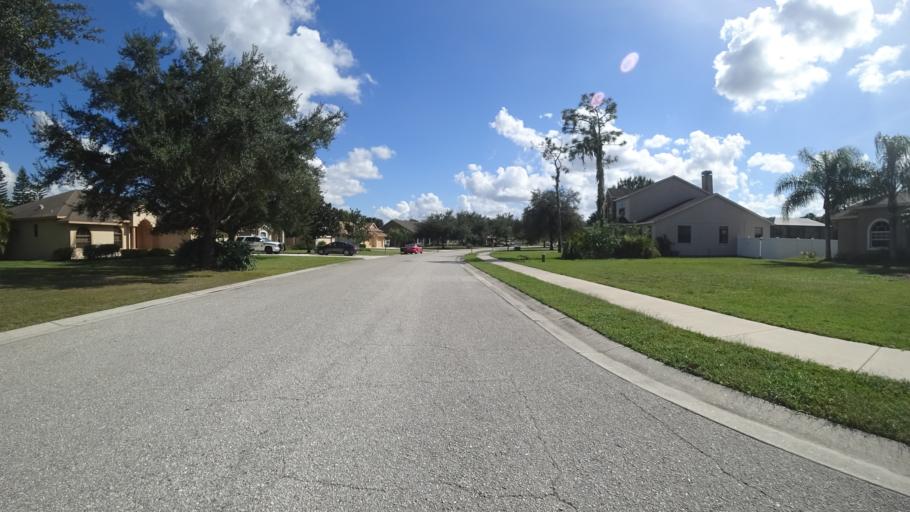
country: US
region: Florida
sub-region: Manatee County
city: Ellenton
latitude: 27.5030
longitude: -82.4002
